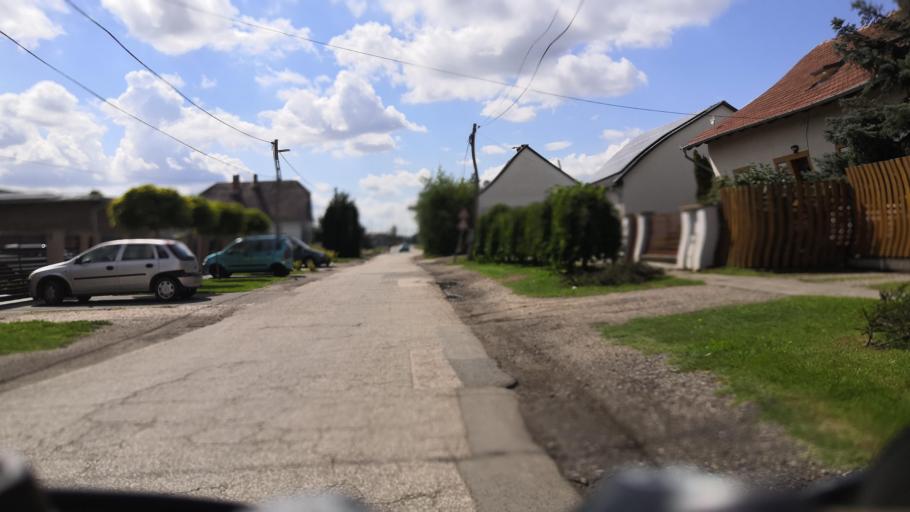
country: HU
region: Csongrad
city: Szeged
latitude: 46.2760
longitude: 20.1090
